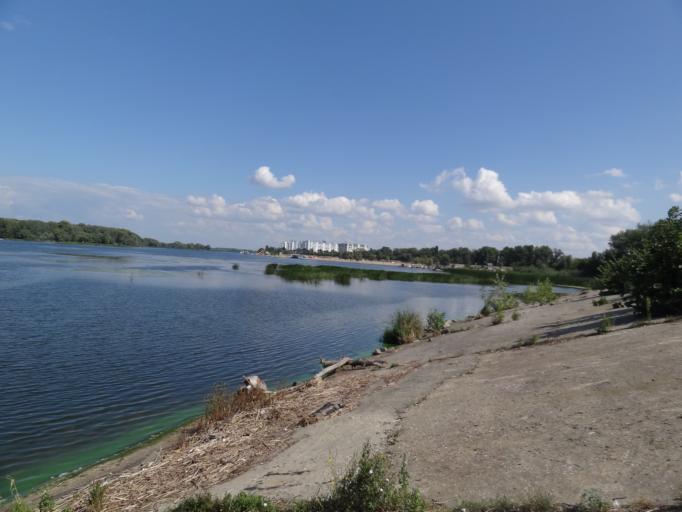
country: RU
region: Saratov
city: Engel's
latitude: 51.5028
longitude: 46.0931
